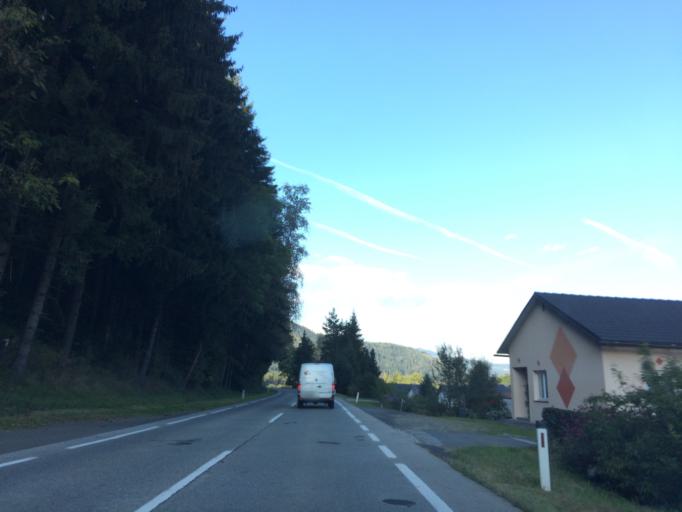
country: AT
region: Styria
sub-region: Politischer Bezirk Leoben
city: Sankt Michael in Obersteiermark
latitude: 47.3428
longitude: 15.0497
